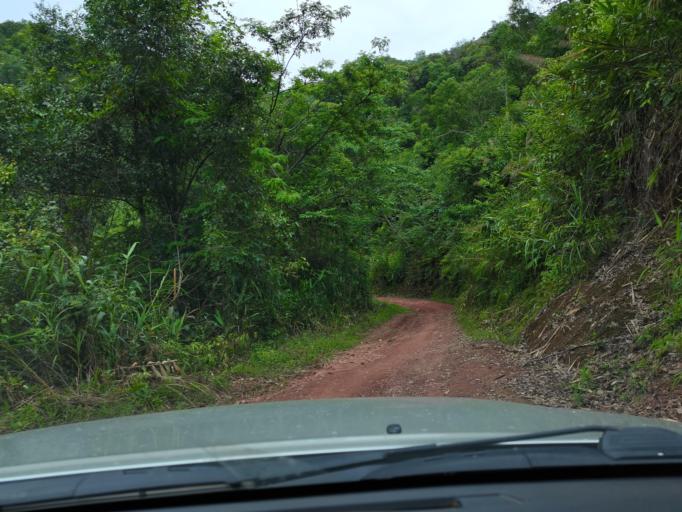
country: LA
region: Loungnamtha
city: Muang Nale
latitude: 20.5093
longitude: 101.0822
